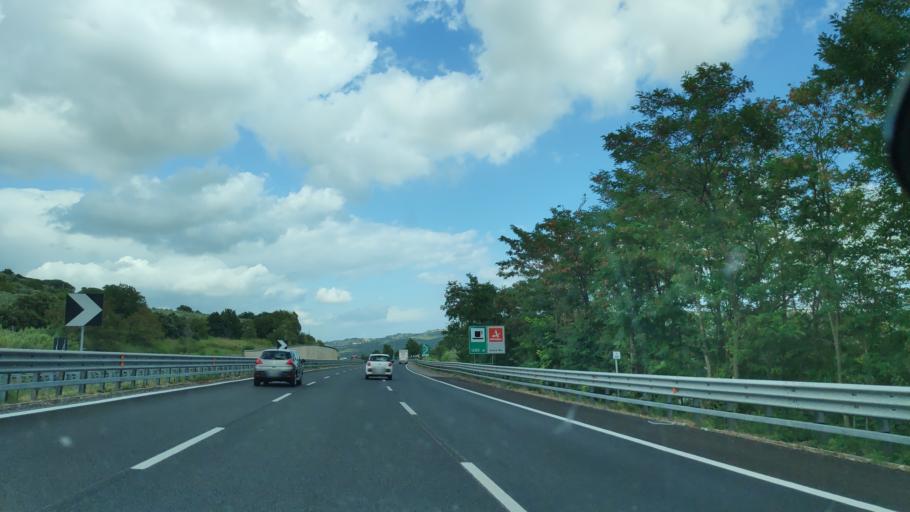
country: IT
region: Campania
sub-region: Provincia di Salerno
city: Quadrivio
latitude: 40.6134
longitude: 15.1445
